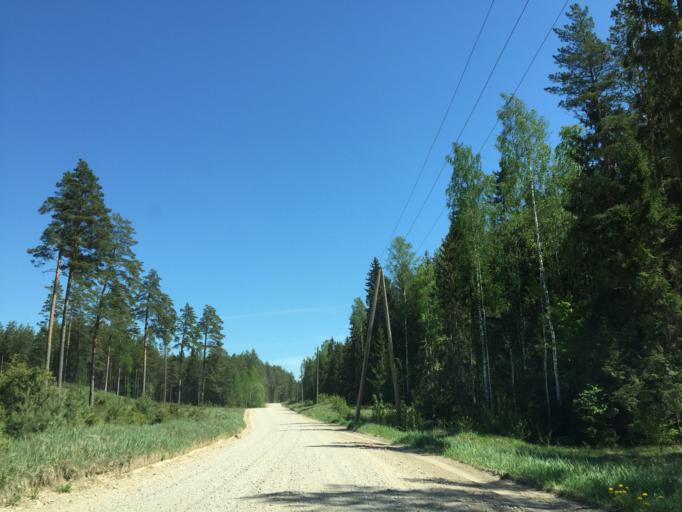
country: LV
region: Ogre
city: Ogre
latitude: 56.7443
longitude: 24.5690
